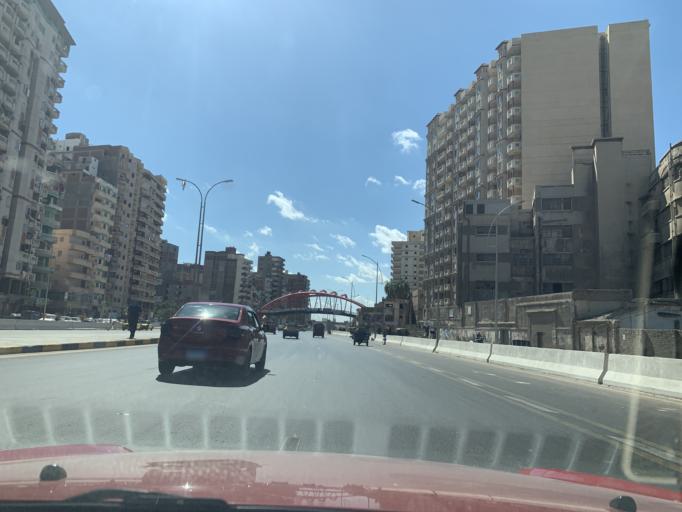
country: EG
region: Alexandria
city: Alexandria
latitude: 31.1955
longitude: 29.9335
